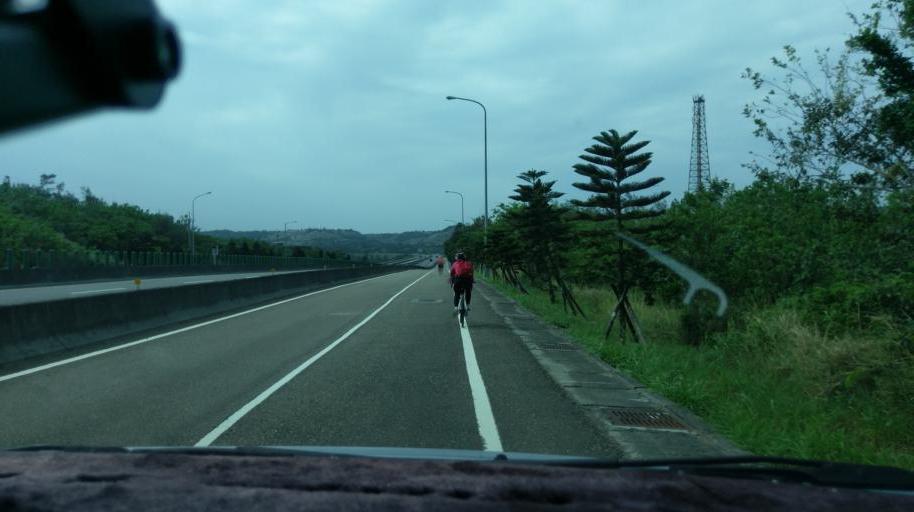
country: TW
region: Taiwan
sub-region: Miaoli
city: Miaoli
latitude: 24.6087
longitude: 120.7509
